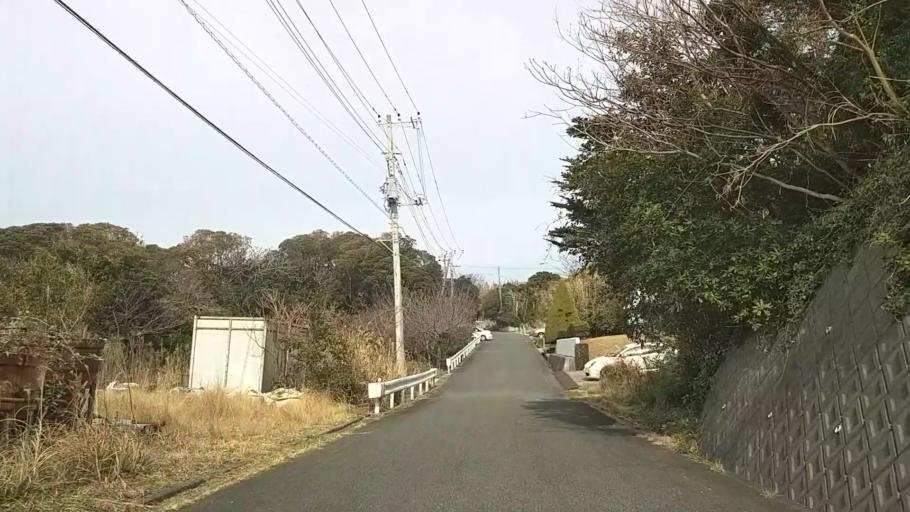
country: JP
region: Shizuoka
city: Shimoda
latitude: 34.6553
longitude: 138.9641
